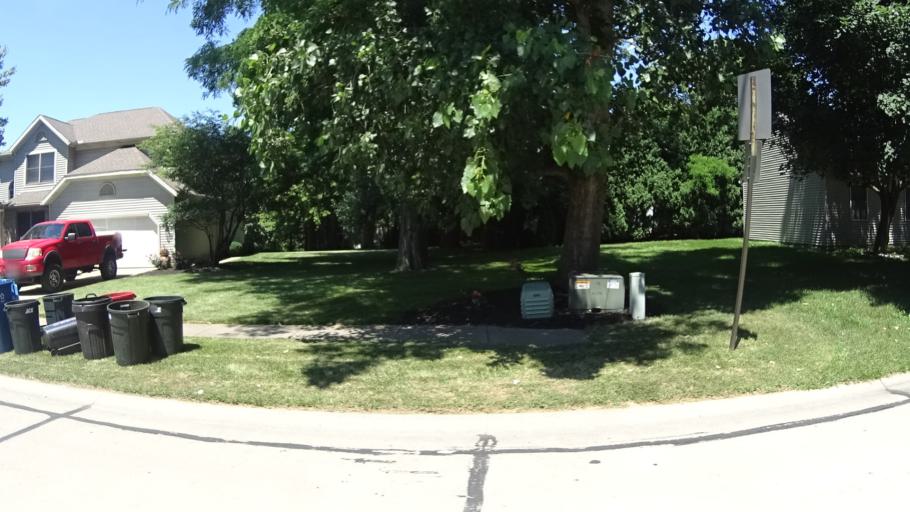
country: US
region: Ohio
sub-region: Erie County
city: Huron
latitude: 41.3938
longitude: -82.5695
